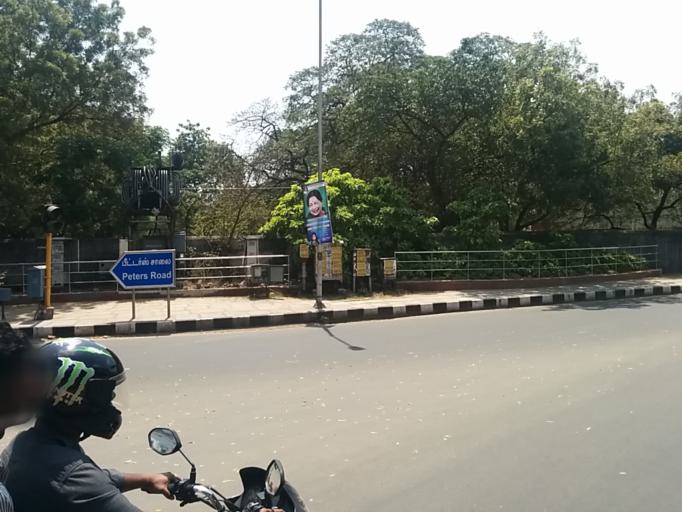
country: IN
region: Tamil Nadu
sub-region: Chennai
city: Chetput
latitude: 13.0548
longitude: 80.2545
